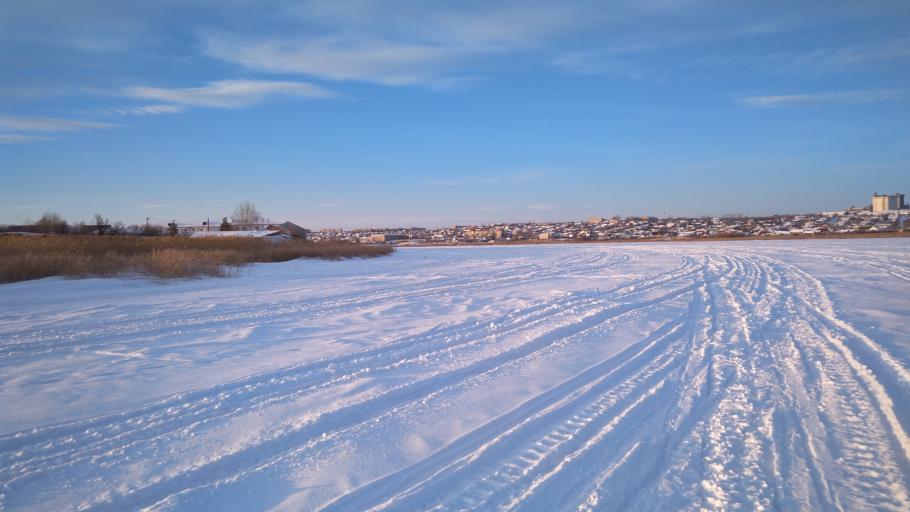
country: RU
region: Chelyabinsk
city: Troitsk
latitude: 54.0859
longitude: 61.5861
